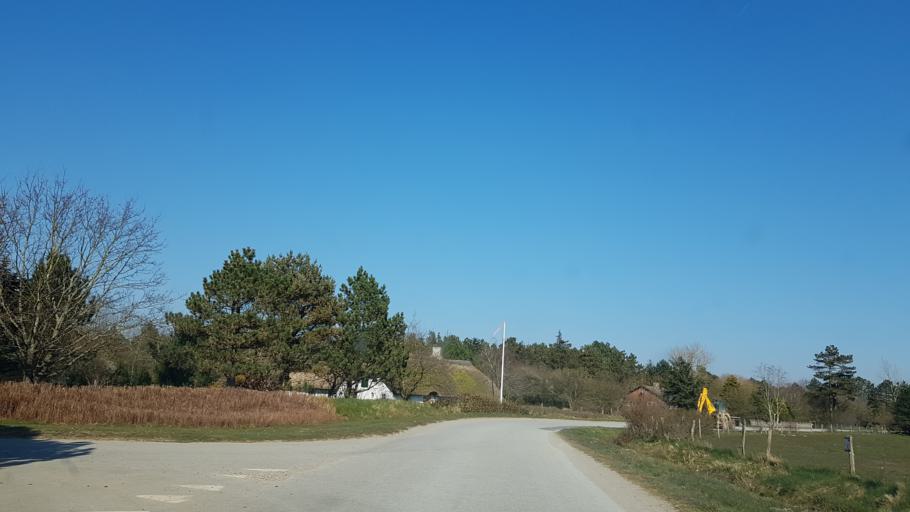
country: DE
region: Schleswig-Holstein
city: List
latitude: 55.0957
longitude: 8.5371
